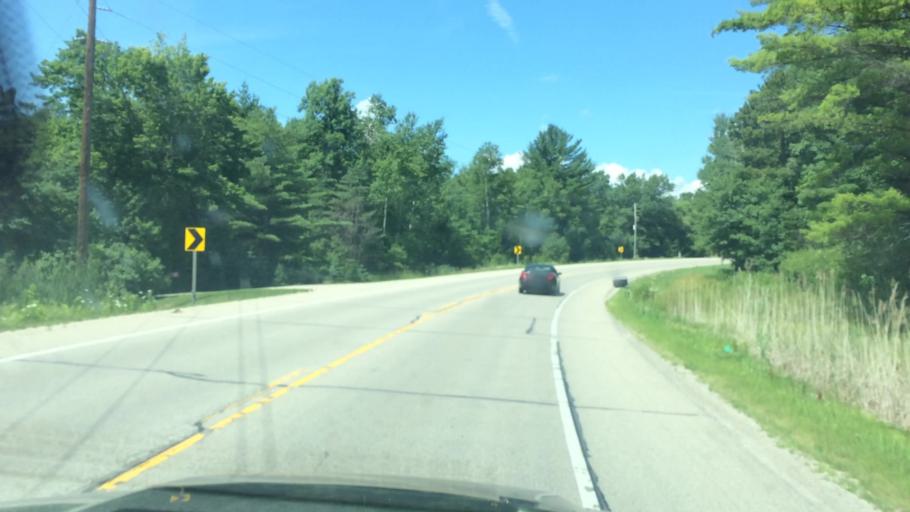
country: US
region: Wisconsin
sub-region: Marinette County
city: Peshtigo
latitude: 45.1005
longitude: -87.7427
